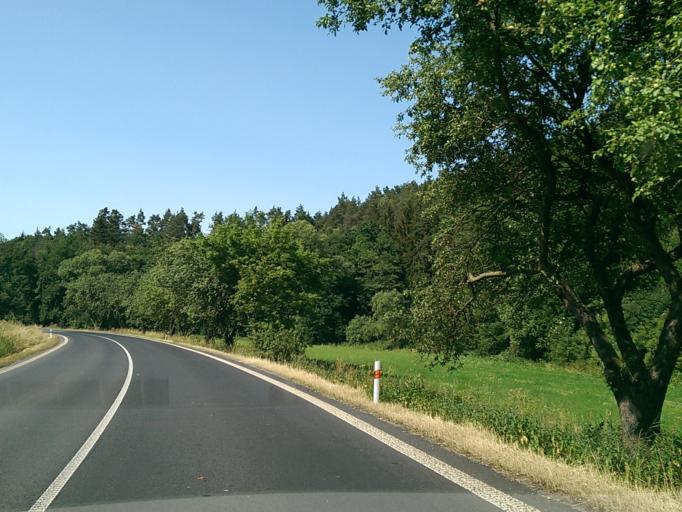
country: CZ
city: Duba
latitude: 50.5131
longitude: 14.4946
